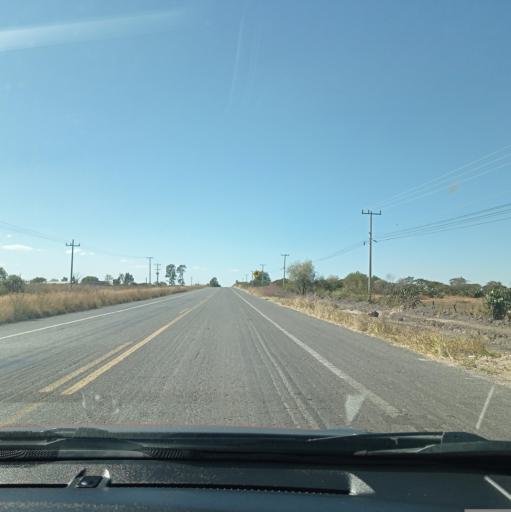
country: MX
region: Jalisco
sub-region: San Julian
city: Colonia Veintitres de Mayo
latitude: 21.0093
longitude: -102.2475
